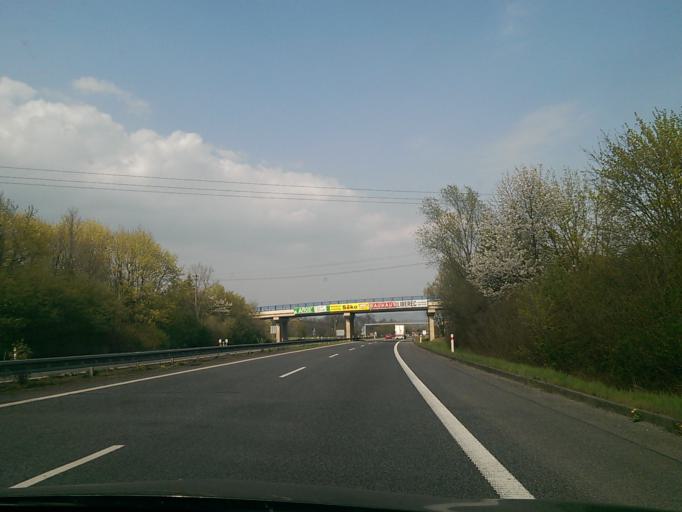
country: CZ
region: Central Bohemia
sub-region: Okres Mlada Boleslav
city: Zd'ar
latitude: 50.5544
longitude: 15.0454
